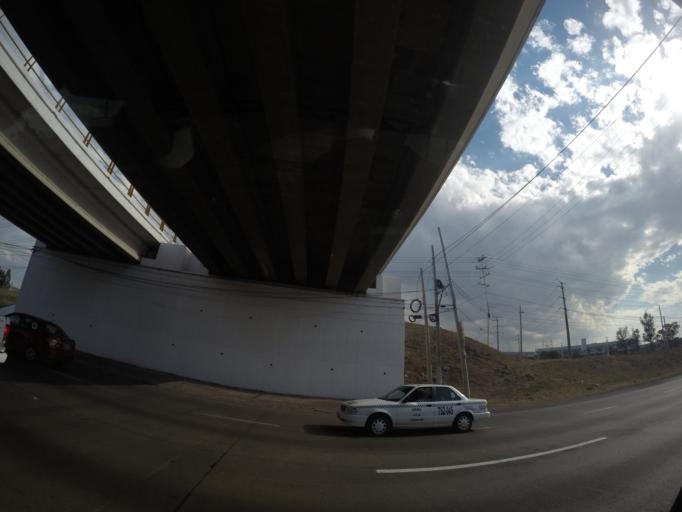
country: MX
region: Queretaro
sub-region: Pedro Escobedo
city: La Palma
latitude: 20.5272
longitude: -100.1776
